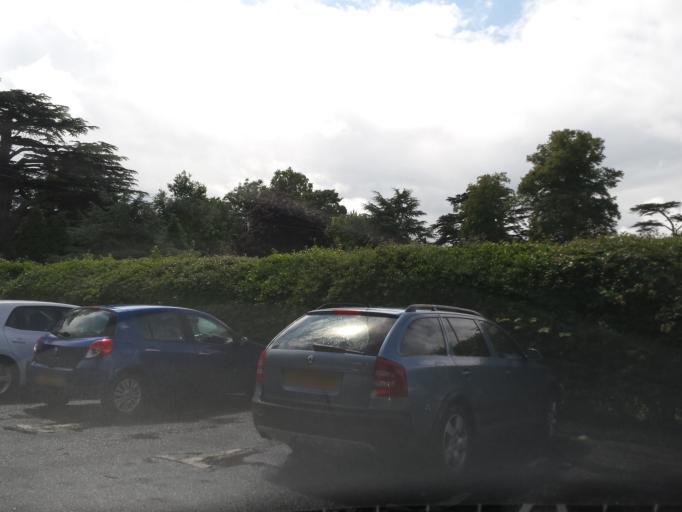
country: GB
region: Scotland
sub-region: The Scottish Borders
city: Saint Boswells
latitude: 55.5788
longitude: -2.6474
